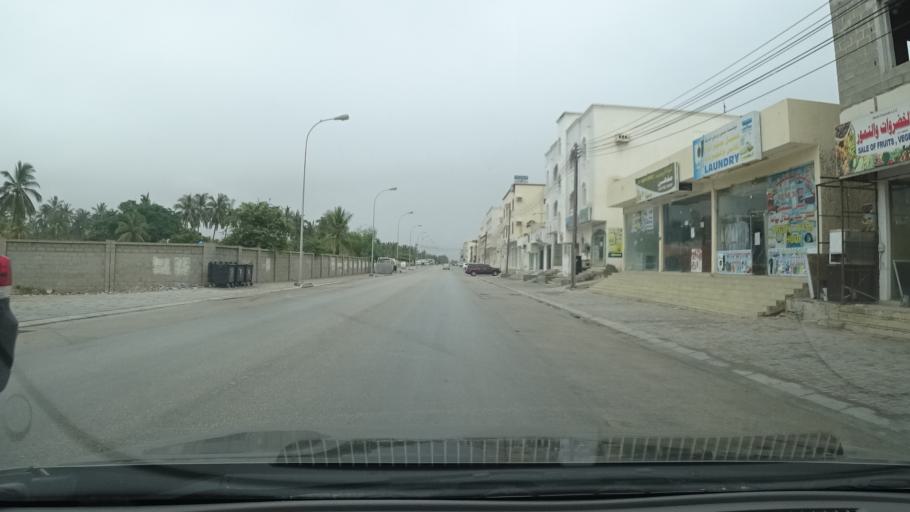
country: OM
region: Zufar
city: Salalah
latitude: 17.0224
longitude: 54.1608
